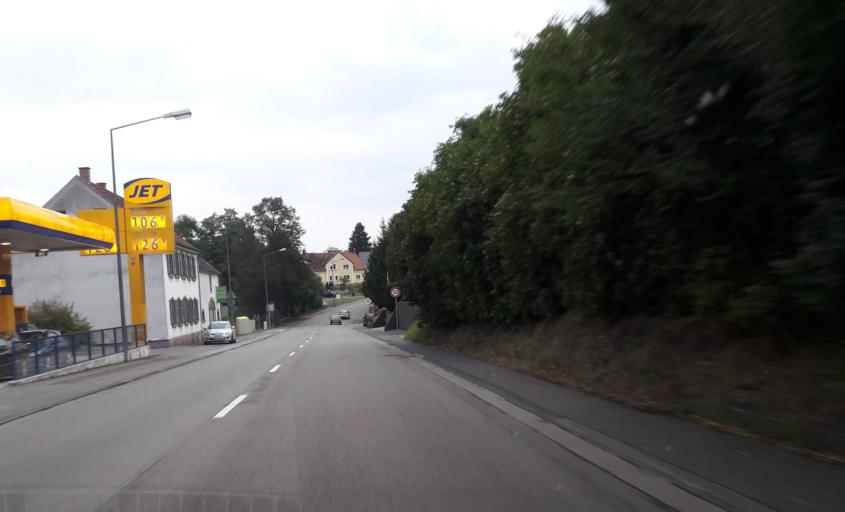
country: DE
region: Saarland
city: Homburg
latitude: 49.2850
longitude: 7.3162
